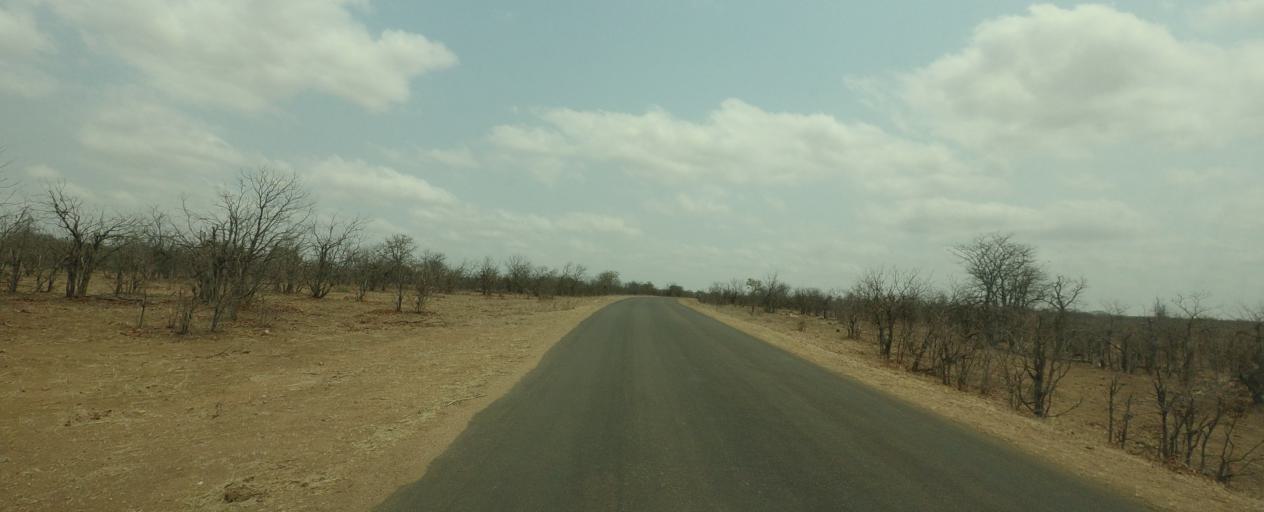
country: ZA
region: Limpopo
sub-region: Mopani District Municipality
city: Phalaborwa
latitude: -23.5520
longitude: 31.4344
